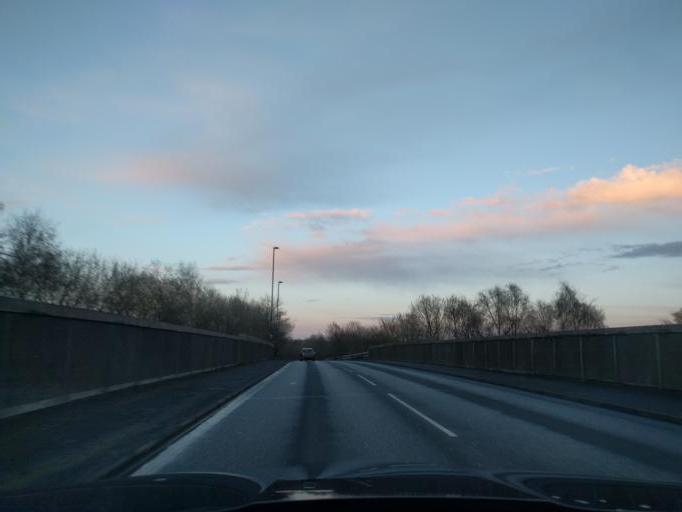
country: GB
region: England
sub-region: Northumberland
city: Seghill
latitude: 55.0392
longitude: -1.5871
